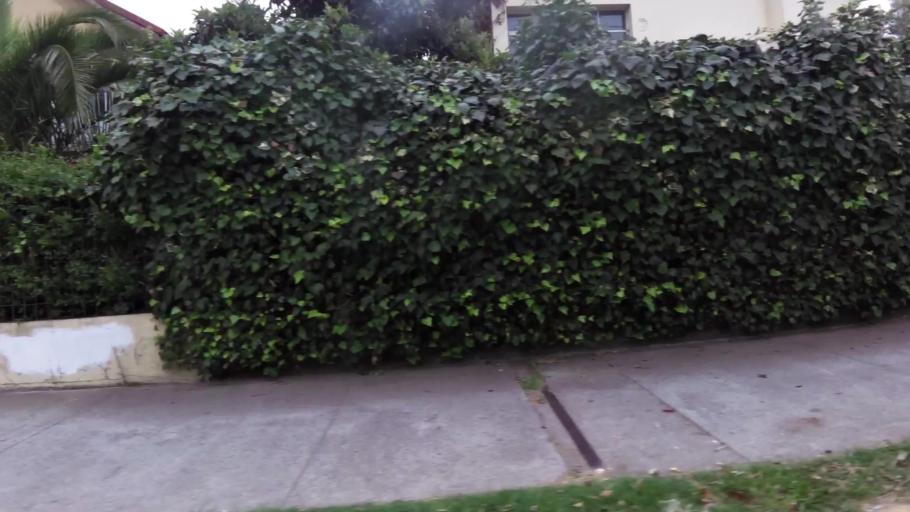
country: CL
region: Biobio
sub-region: Provincia de Concepcion
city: Concepcion
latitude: -36.8290
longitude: -73.0403
